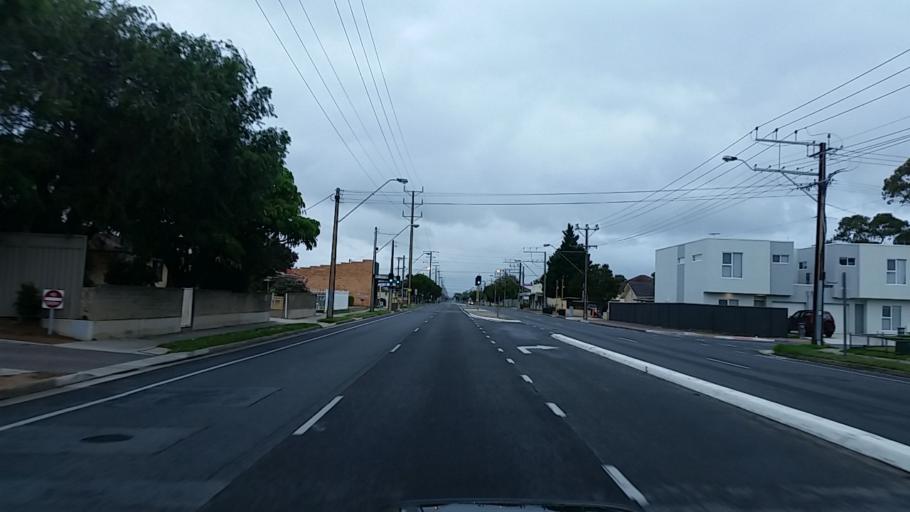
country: AU
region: South Australia
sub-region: Charles Sturt
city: Royal Park
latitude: -34.8842
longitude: 138.5131
